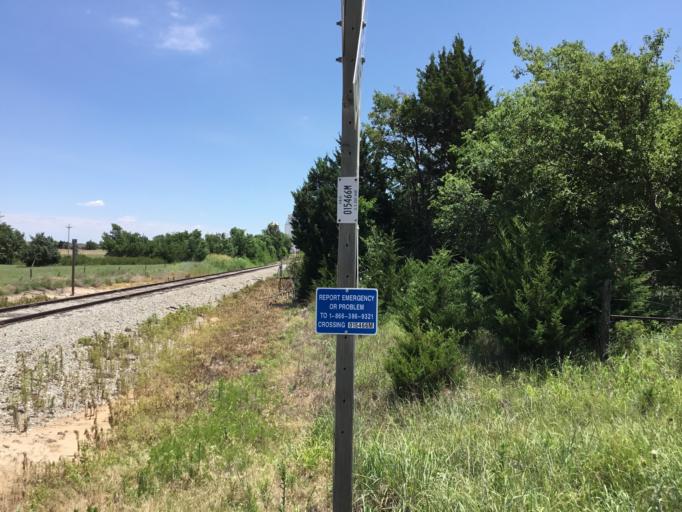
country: US
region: Kansas
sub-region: Barber County
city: Medicine Lodge
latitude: 37.4415
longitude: -98.4281
